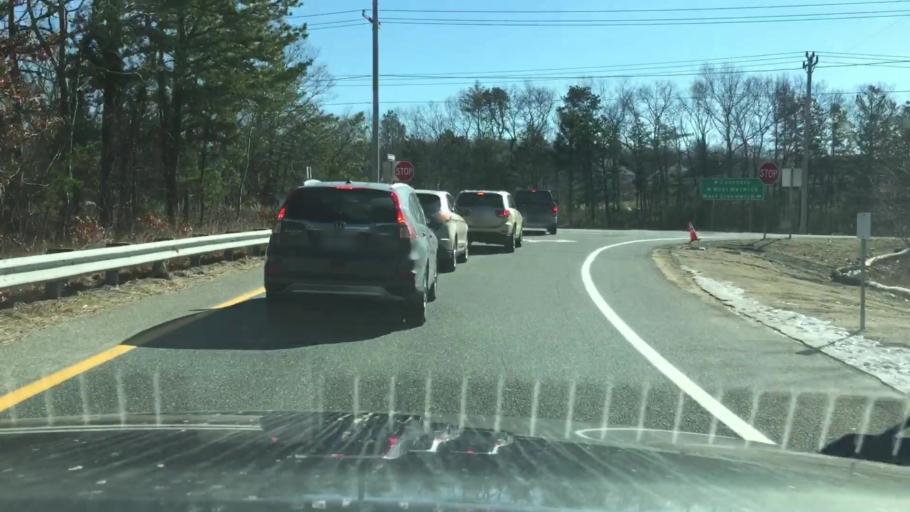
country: US
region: Rhode Island
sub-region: Kent County
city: West Warwick
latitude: 41.6589
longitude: -71.5495
